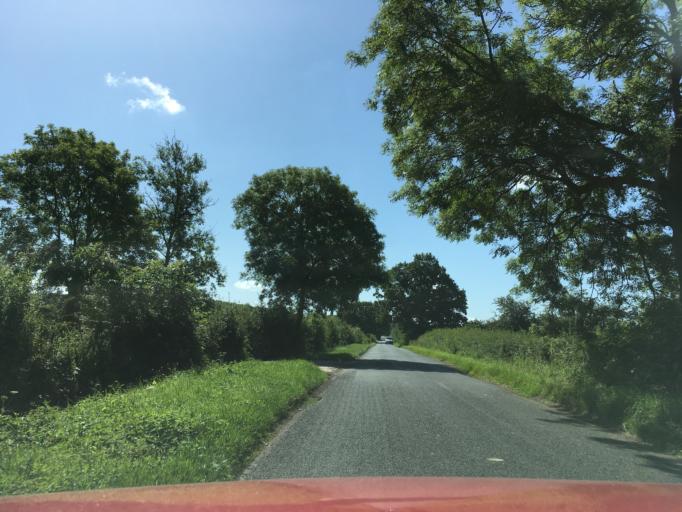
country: GB
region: England
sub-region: Milton Keynes
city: Calverton
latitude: 51.9939
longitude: -0.8604
